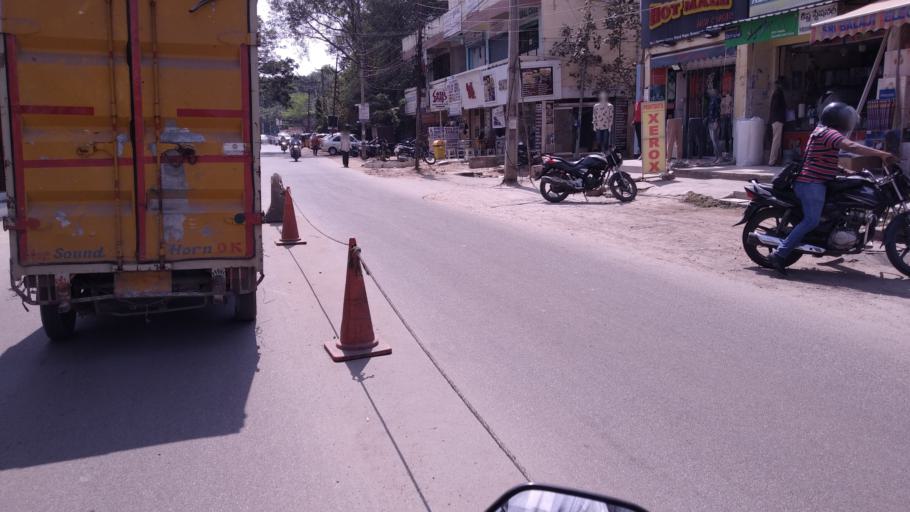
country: IN
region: Telangana
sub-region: Rangareddi
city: Quthbullapur
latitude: 17.4643
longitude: 78.4835
